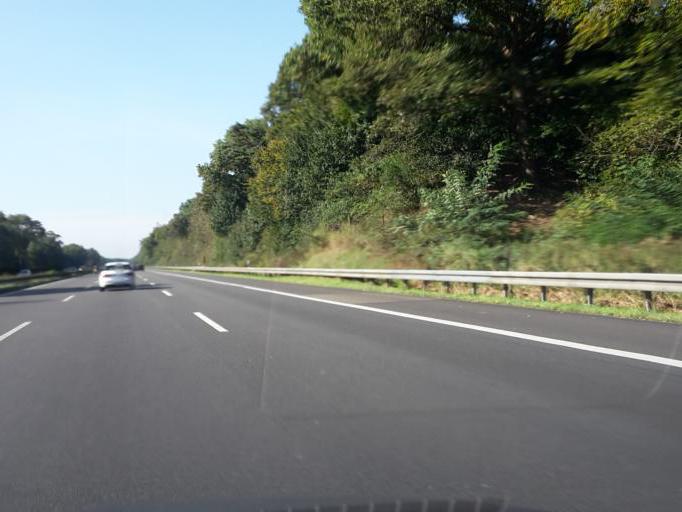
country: DE
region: North Rhine-Westphalia
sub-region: Regierungsbezirk Koln
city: Rosrath
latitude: 50.9016
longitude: 7.1414
